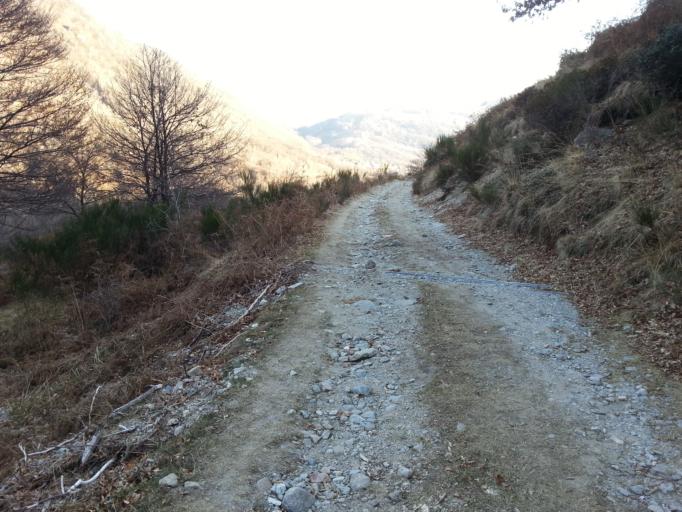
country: CH
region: Ticino
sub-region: Lugano District
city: Gravesano
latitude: 46.0601
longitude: 8.8792
